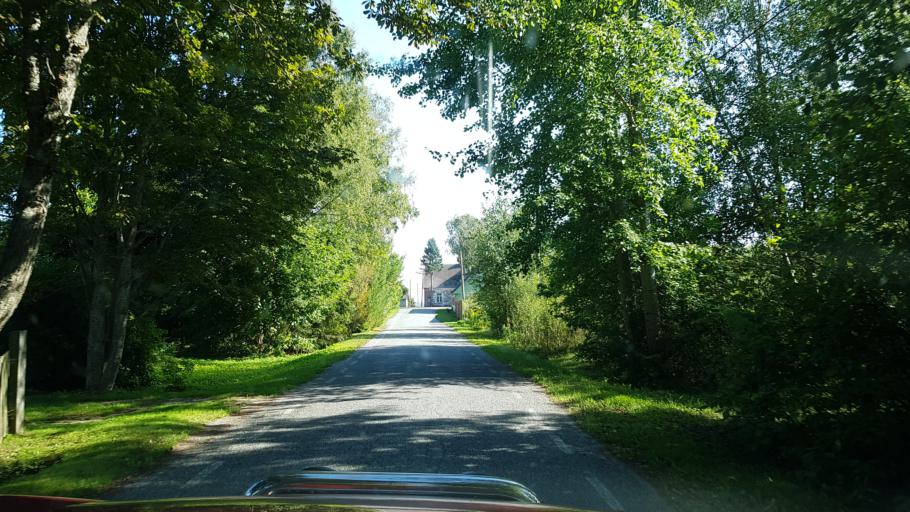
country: EE
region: Polvamaa
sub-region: Raepina vald
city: Rapina
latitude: 58.2339
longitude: 27.4729
